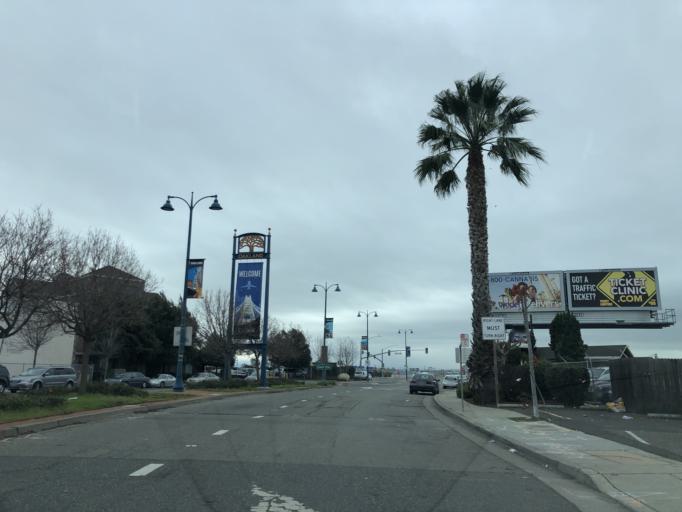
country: US
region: California
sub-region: Alameda County
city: San Leandro
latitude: 37.7243
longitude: -122.1979
